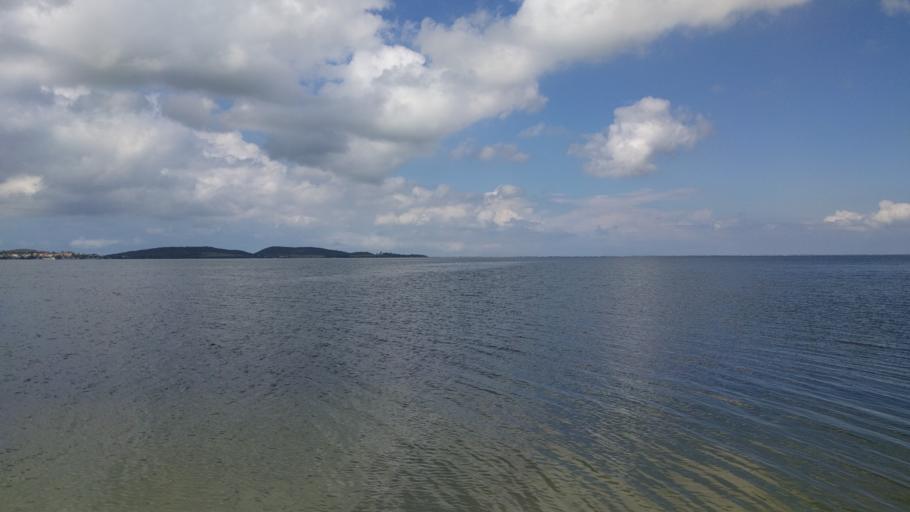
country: BR
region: Rio de Janeiro
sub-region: Sao Pedro Da Aldeia
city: Sao Pedro da Aldeia
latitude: -22.8432
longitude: -42.1259
